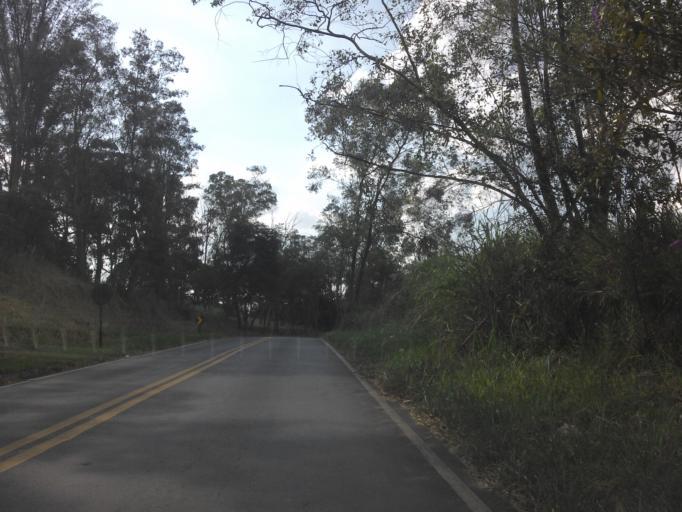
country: BR
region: Sao Paulo
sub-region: Vinhedo
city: Vinhedo
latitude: -23.0100
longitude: -47.0034
